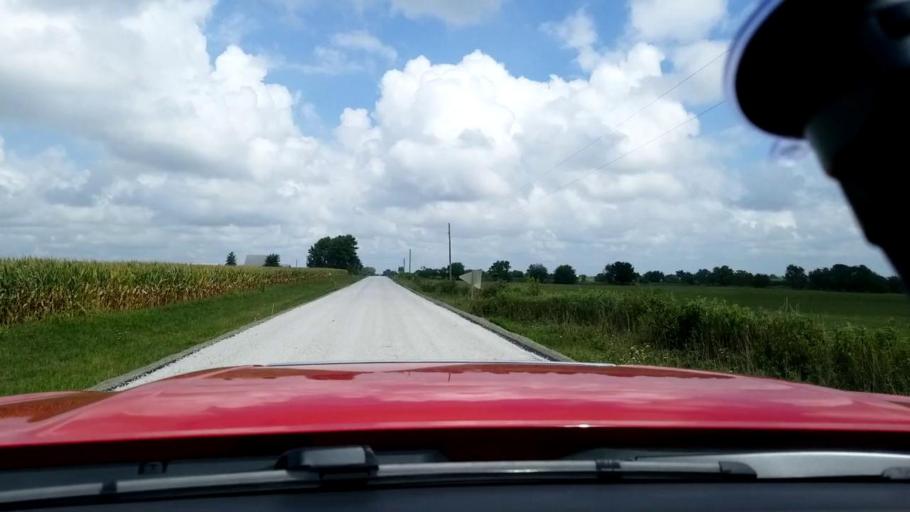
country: US
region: Iowa
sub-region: Decatur County
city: Lamoni
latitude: 40.6250
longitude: -94.0534
